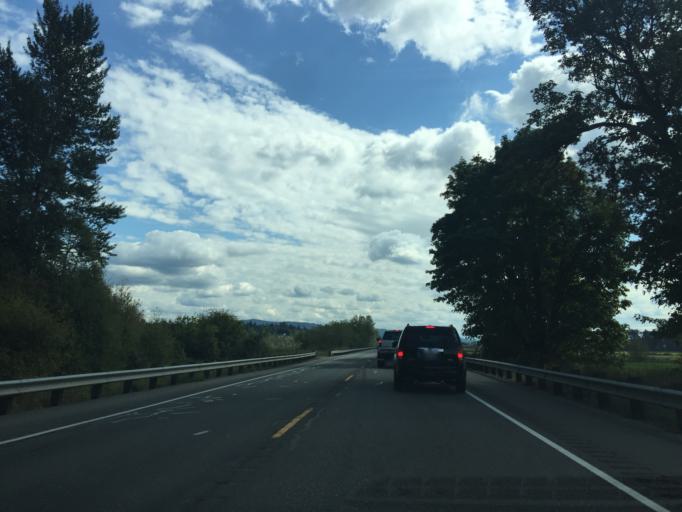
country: US
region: Washington
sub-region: Snohomish County
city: Three Lakes
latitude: 47.8922
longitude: -122.0295
